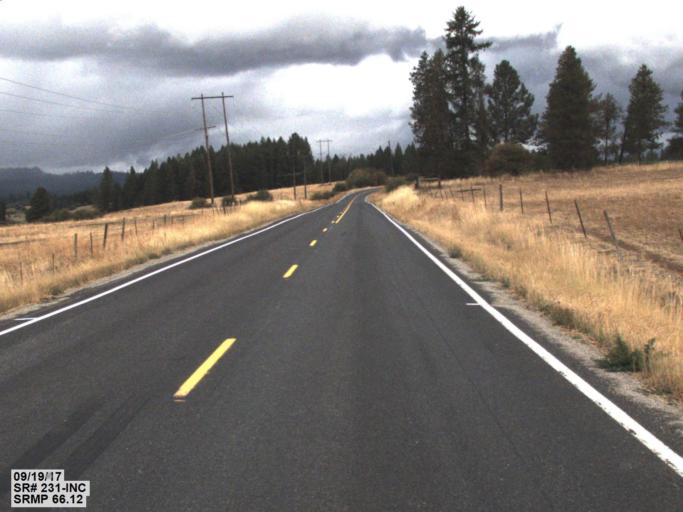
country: US
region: Washington
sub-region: Stevens County
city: Chewelah
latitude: 48.1016
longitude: -117.7578
